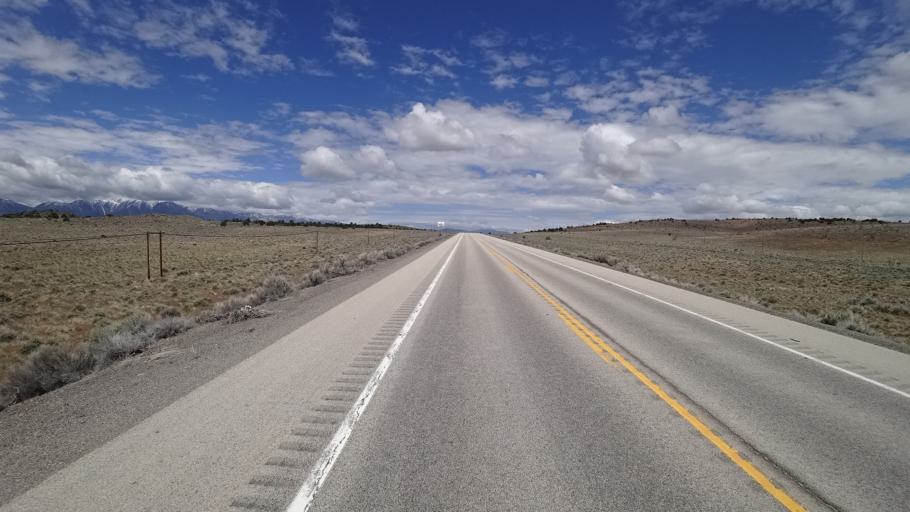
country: US
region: Nevada
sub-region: Douglas County
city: Gardnerville Ranchos
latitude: 38.8599
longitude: -119.6691
